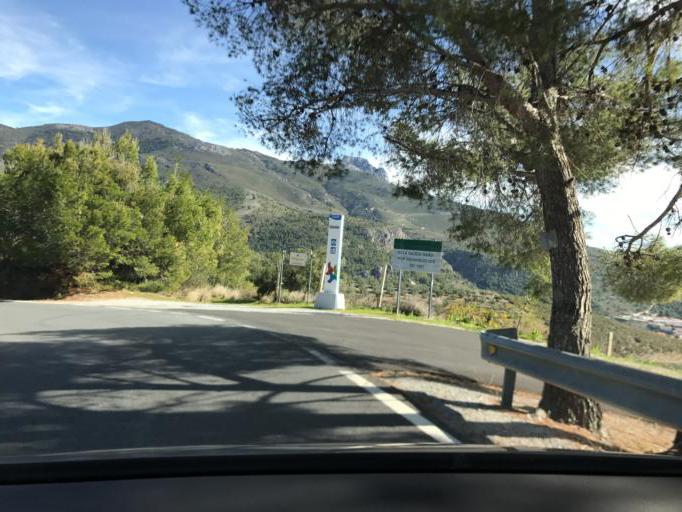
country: ES
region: Andalusia
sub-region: Provincia de Granada
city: Otivar
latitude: 36.8220
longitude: -3.6932
